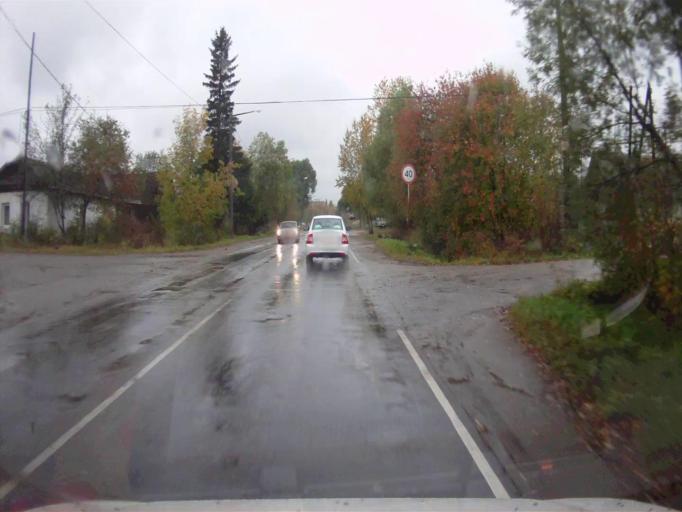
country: RU
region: Chelyabinsk
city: Kyshtym
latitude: 55.7209
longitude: 60.5397
